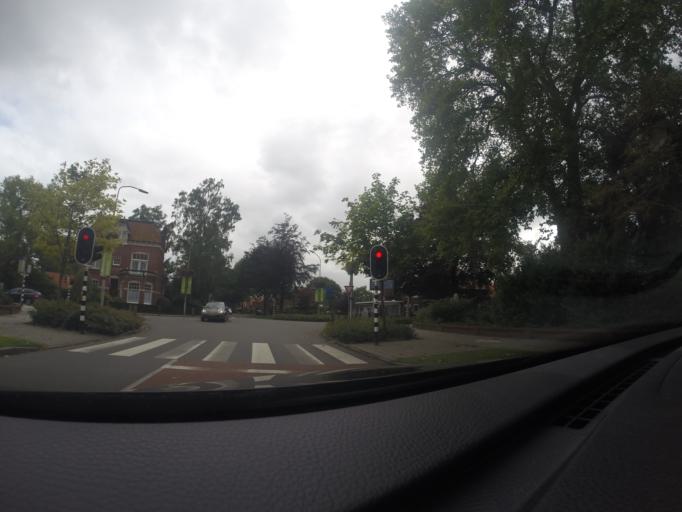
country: NL
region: Overijssel
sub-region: Gemeente Hof van Twente
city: Markelo
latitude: 52.2345
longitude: 6.4974
